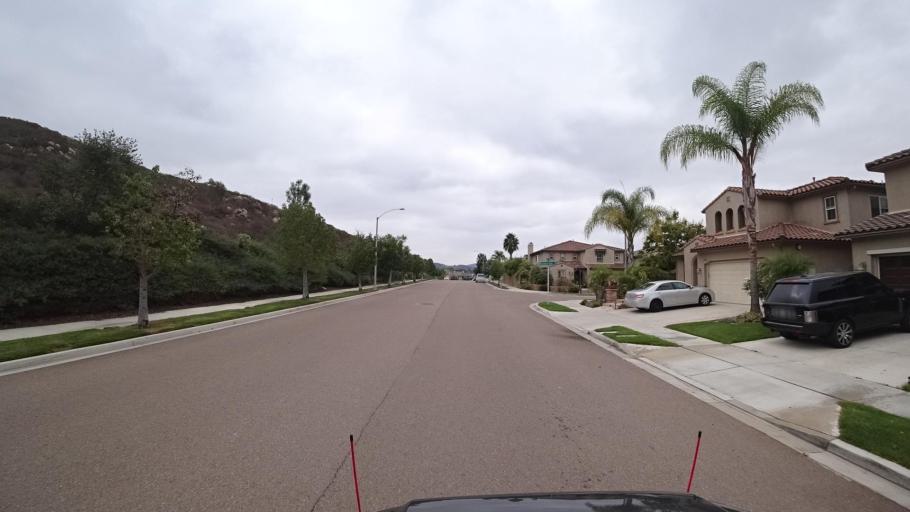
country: US
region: California
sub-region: San Diego County
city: Fairbanks Ranch
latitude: 33.0327
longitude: -117.1094
